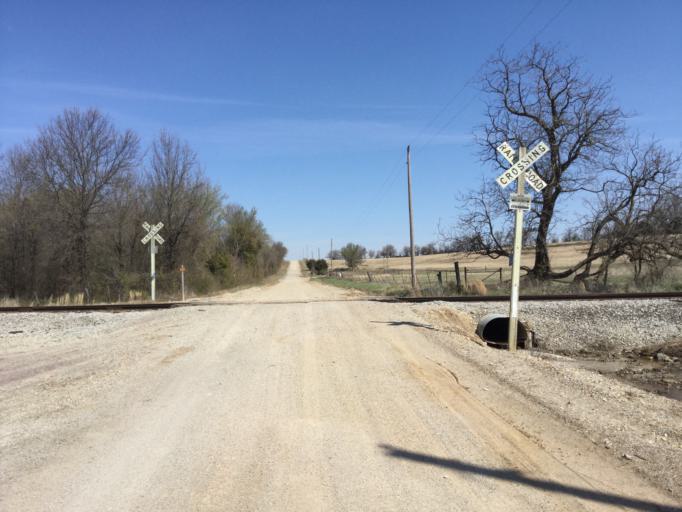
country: US
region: Kansas
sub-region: Cherokee County
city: Columbus
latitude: 37.1399
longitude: -94.7954
